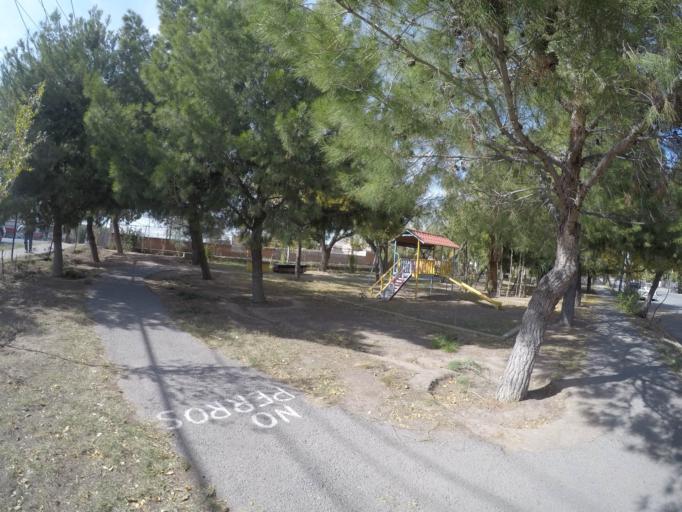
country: MX
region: Chihuahua
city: Ciudad Juarez
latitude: 31.7331
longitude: -106.4353
